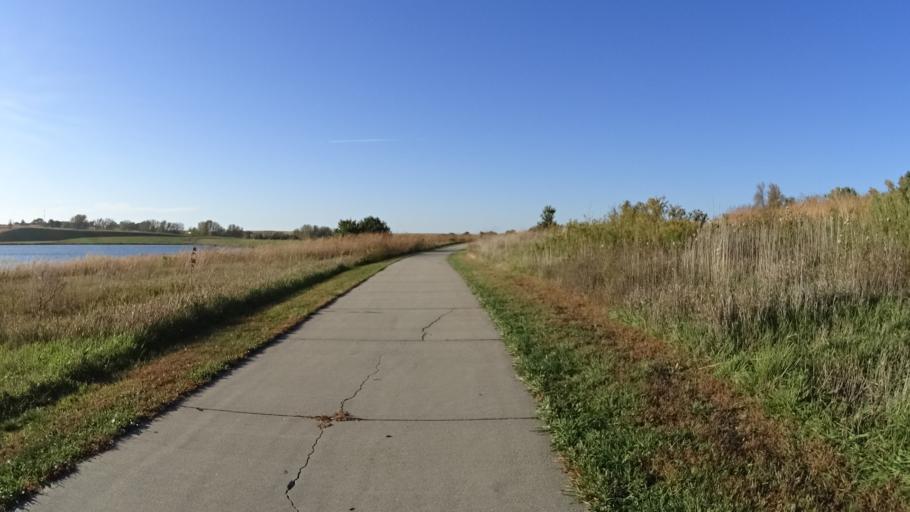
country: US
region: Nebraska
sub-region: Sarpy County
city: Papillion
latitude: 41.1423
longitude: -96.0653
